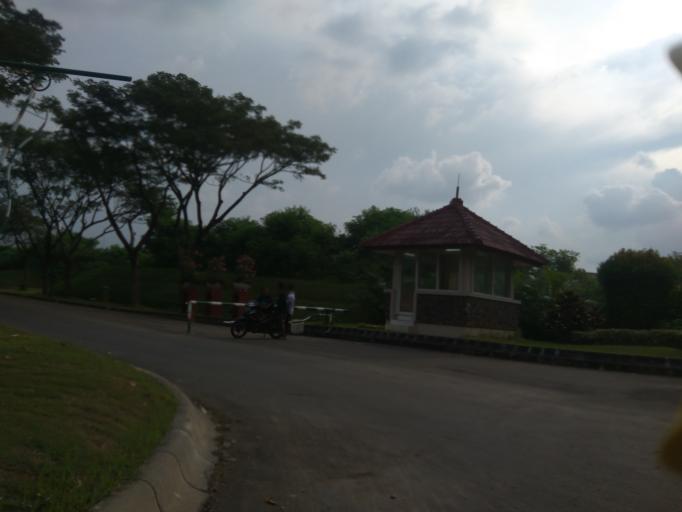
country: ID
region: Central Java
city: Semarang
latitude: -7.0306
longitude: 110.4361
